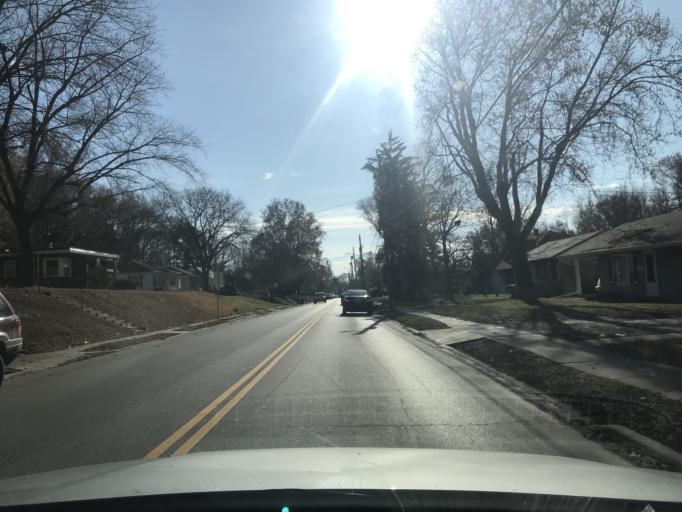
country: US
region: Iowa
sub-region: Scott County
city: Davenport
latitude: 41.5258
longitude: -90.6159
